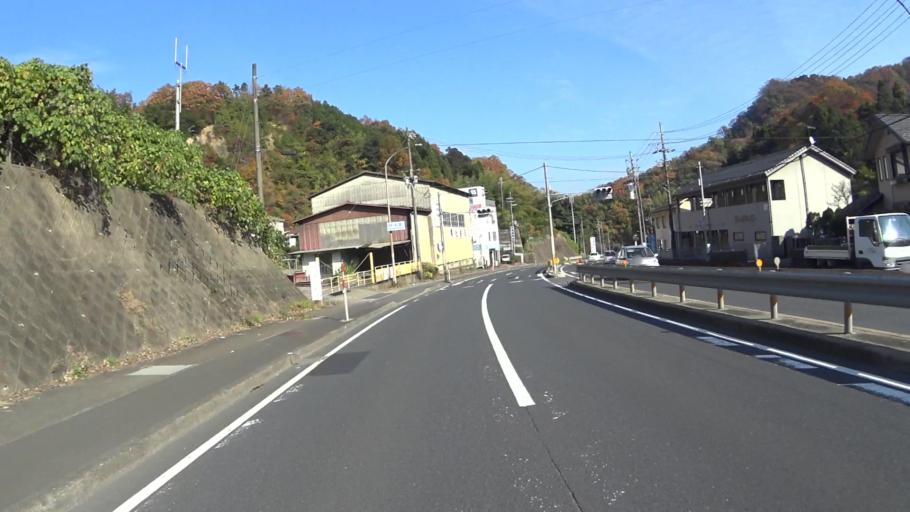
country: JP
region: Kyoto
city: Maizuru
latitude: 35.4617
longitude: 135.3586
